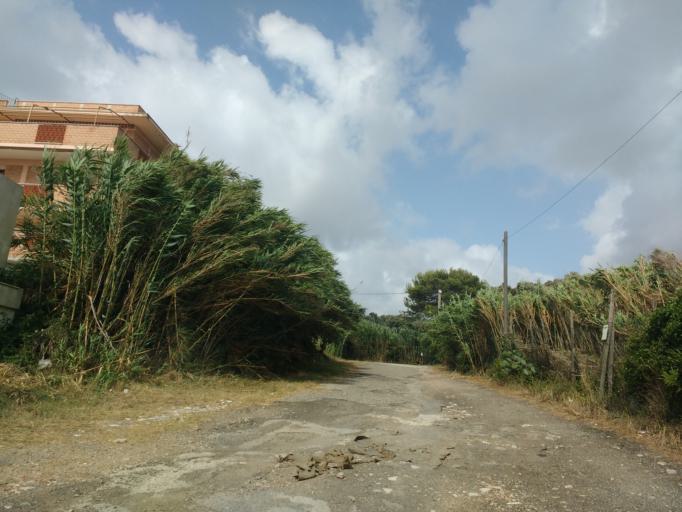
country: IT
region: Latium
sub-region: Citta metropolitana di Roma Capitale
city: Lavinio
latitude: 41.4904
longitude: 12.5898
